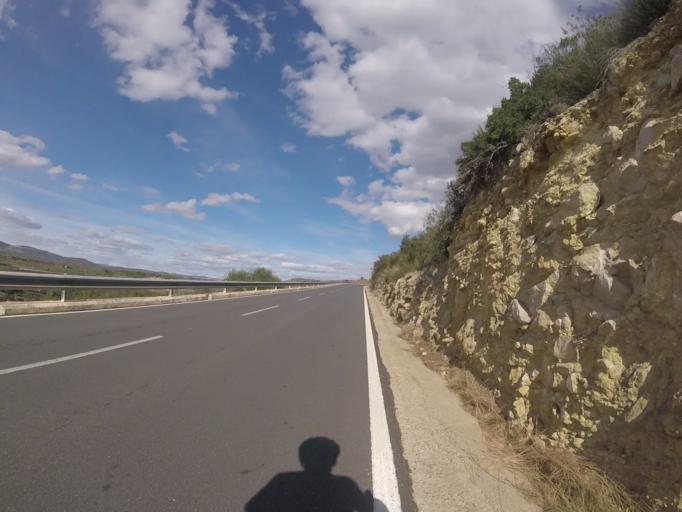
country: ES
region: Valencia
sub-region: Provincia de Castello
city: Cuevas de Vinroma
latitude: 40.3162
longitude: 0.1292
